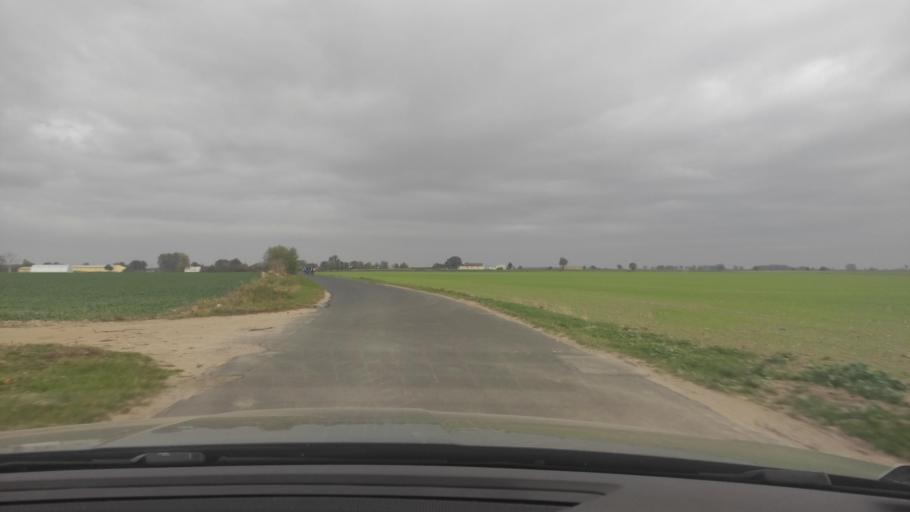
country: PL
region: Greater Poland Voivodeship
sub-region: Powiat poznanski
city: Kostrzyn
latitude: 52.4438
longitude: 17.1973
